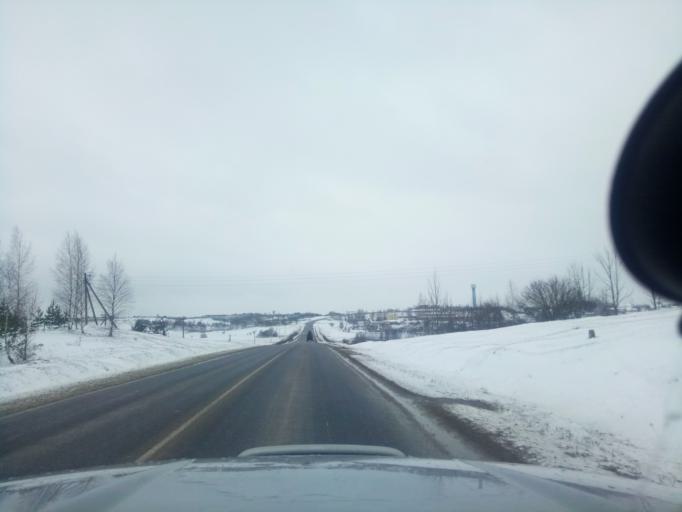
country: BY
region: Minsk
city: Kapyl'
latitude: 53.1416
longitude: 27.0826
